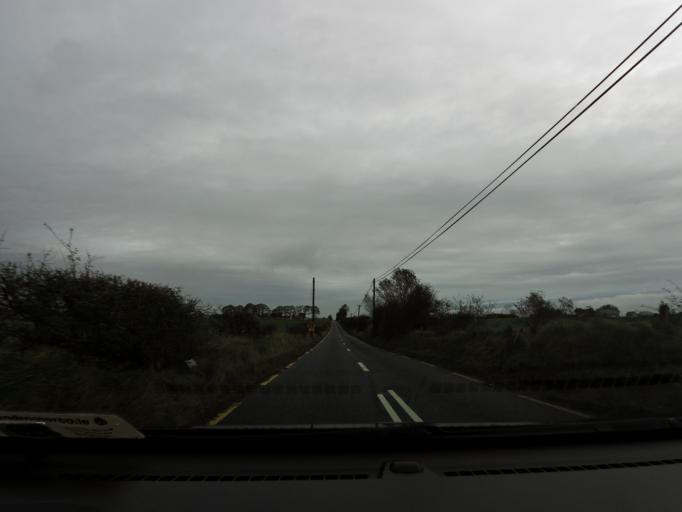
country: IE
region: Connaught
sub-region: County Galway
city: Tuam
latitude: 53.5838
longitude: -8.7798
